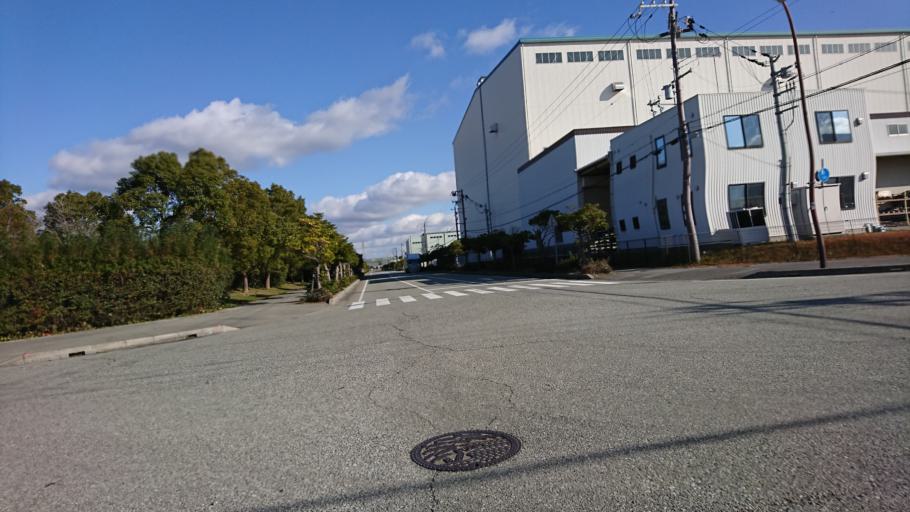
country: JP
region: Hyogo
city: Kakogawacho-honmachi
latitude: 34.7526
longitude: 134.7840
